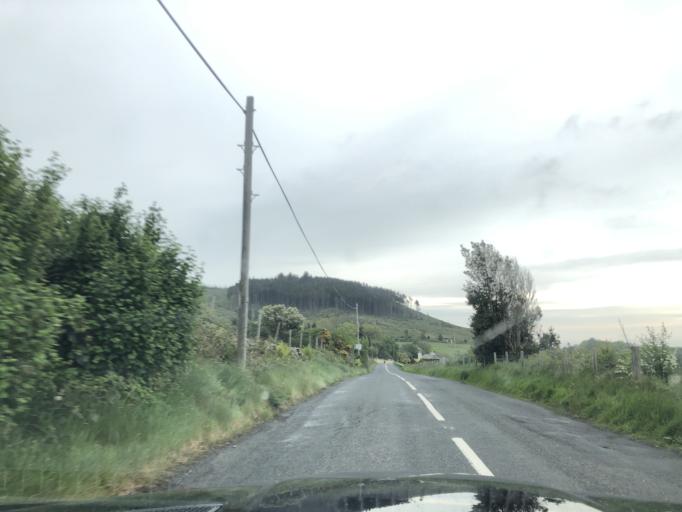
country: GB
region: Northern Ireland
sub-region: Down District
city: Castlewellan
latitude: 54.2216
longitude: -5.9823
